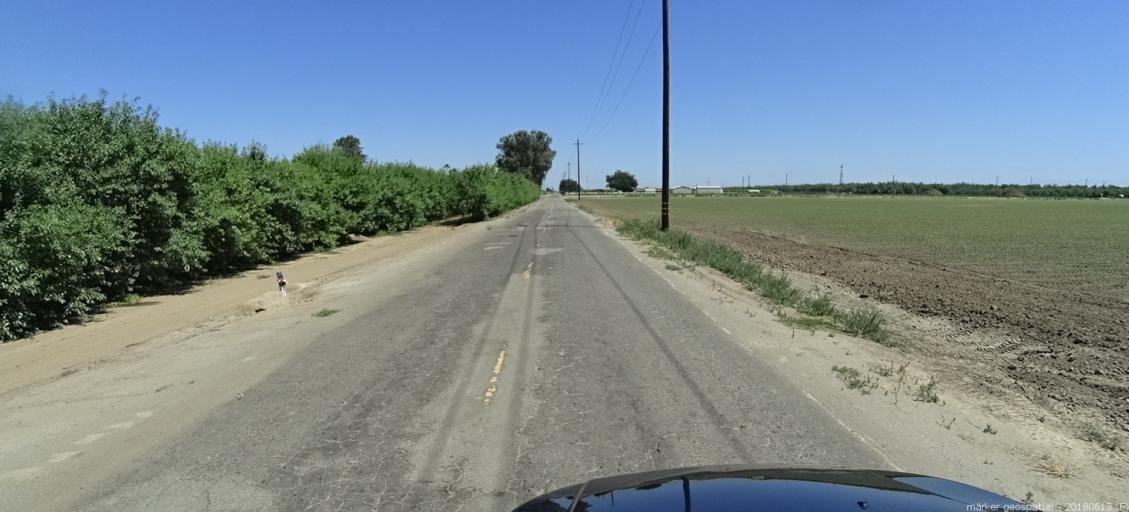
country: US
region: California
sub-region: Madera County
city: Chowchilla
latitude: 37.0766
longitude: -120.3288
